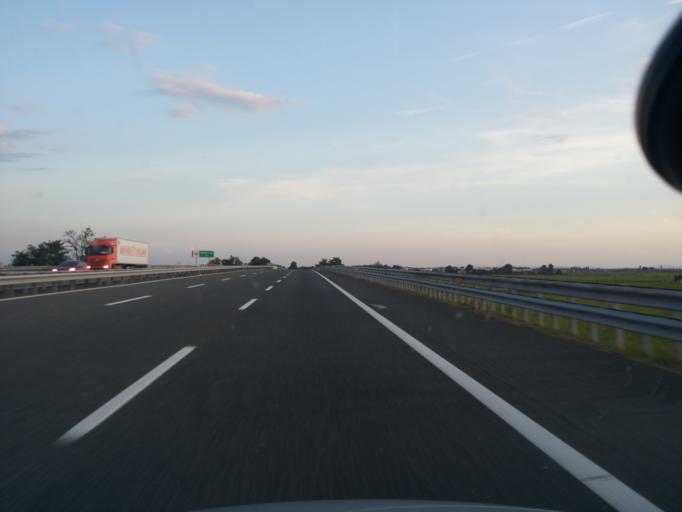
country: IT
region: Piedmont
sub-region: Provincia di Novara
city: Casalvolone
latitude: 45.3839
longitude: 8.4850
